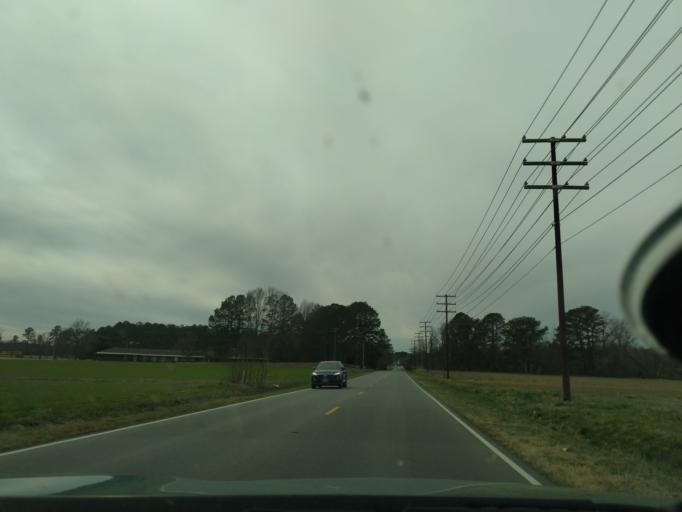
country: US
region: North Carolina
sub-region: Edgecombe County
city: Tarboro
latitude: 35.8951
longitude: -77.5769
